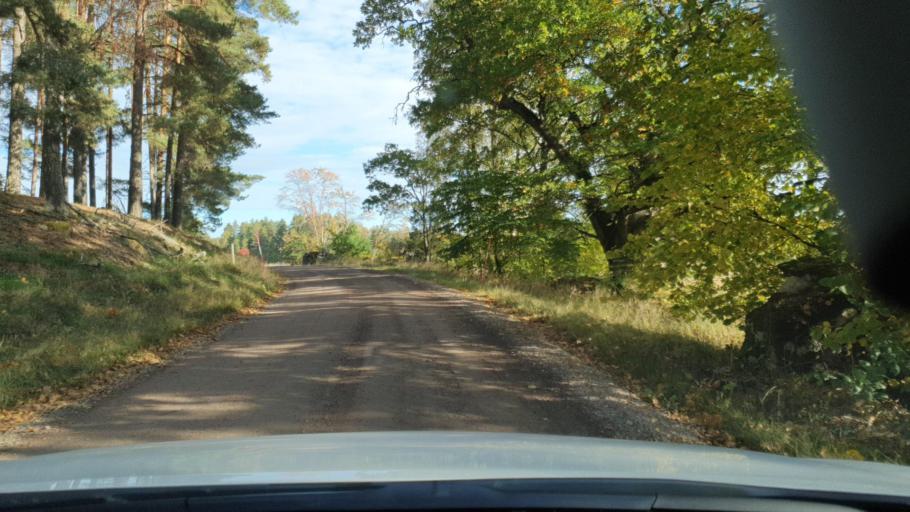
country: SE
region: Kalmar
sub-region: Hultsfreds Kommun
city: Malilla
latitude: 57.3286
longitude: 15.8105
